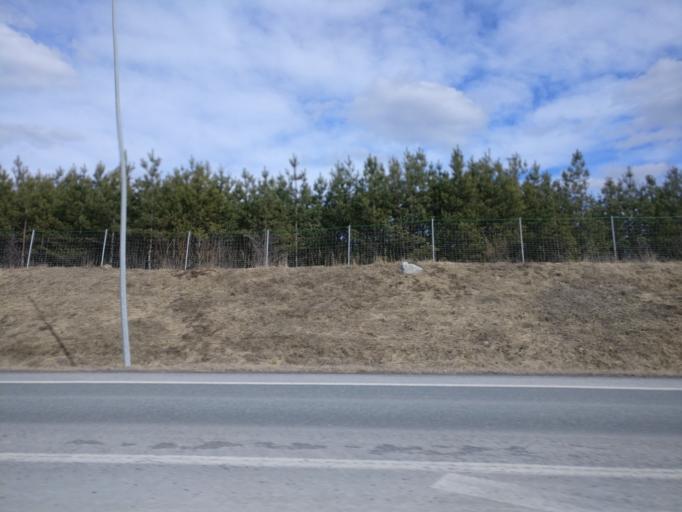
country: FI
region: Pirkanmaa
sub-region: Tampere
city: Lempaeaelae
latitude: 61.3298
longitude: 23.8013
